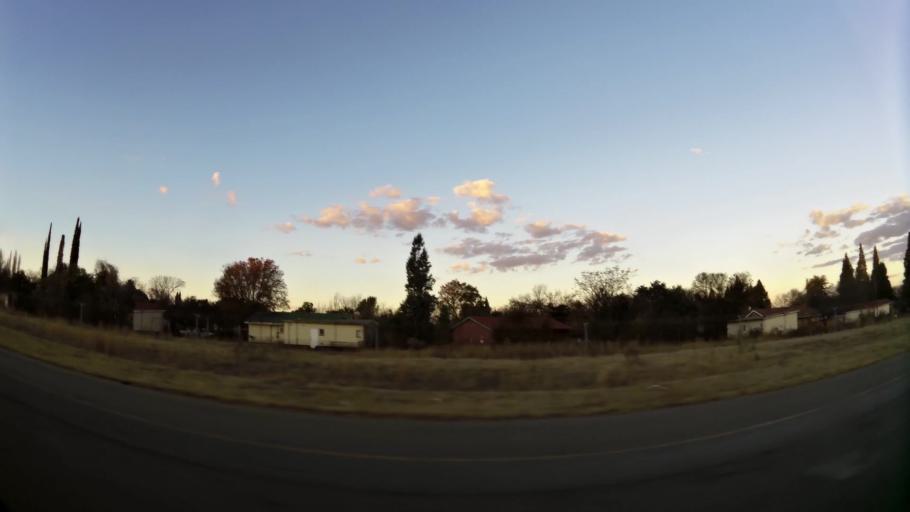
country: ZA
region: North-West
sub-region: Dr Kenneth Kaunda District Municipality
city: Potchefstroom
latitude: -26.6852
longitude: 27.0766
